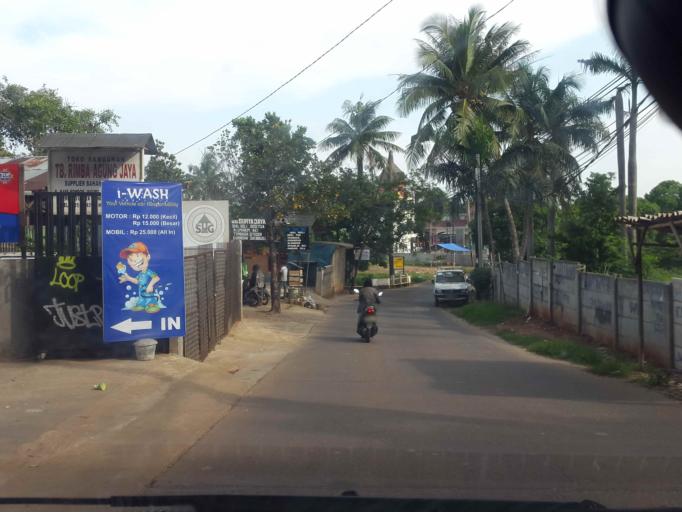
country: ID
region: West Java
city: Ciputat
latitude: -6.2568
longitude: 106.6755
